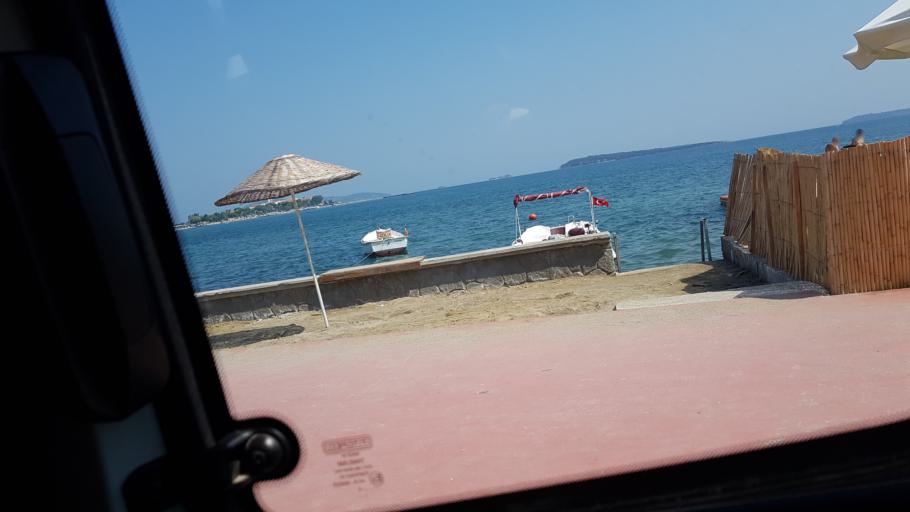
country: TR
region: Izmir
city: Urla
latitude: 38.3902
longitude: 26.7512
